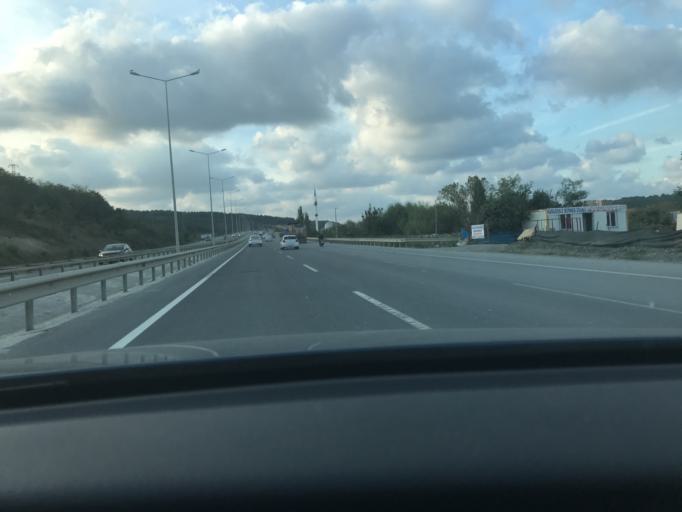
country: TR
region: Istanbul
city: Kemerburgaz
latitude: 41.1789
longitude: 28.8763
